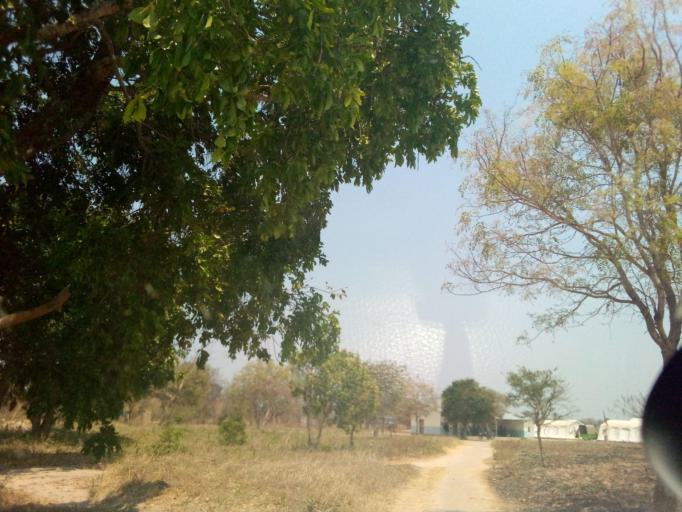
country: ZM
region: Copperbelt
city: Kataba
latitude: -12.2395
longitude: 30.3143
